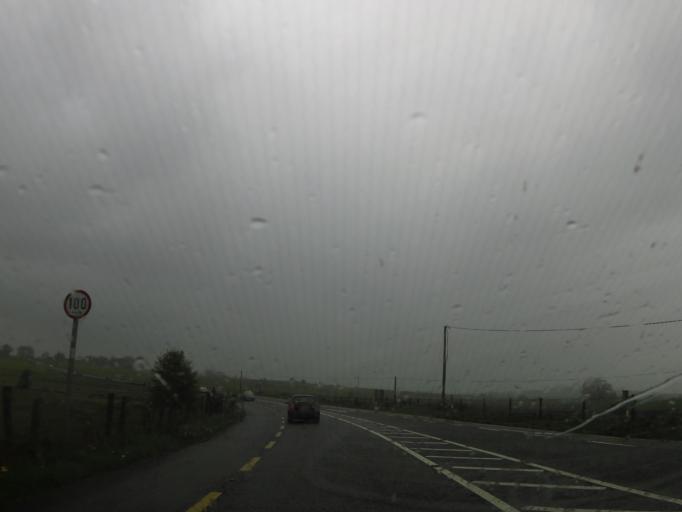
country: IE
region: Connaught
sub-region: County Galway
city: Tuam
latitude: 53.4923
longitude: -8.9077
